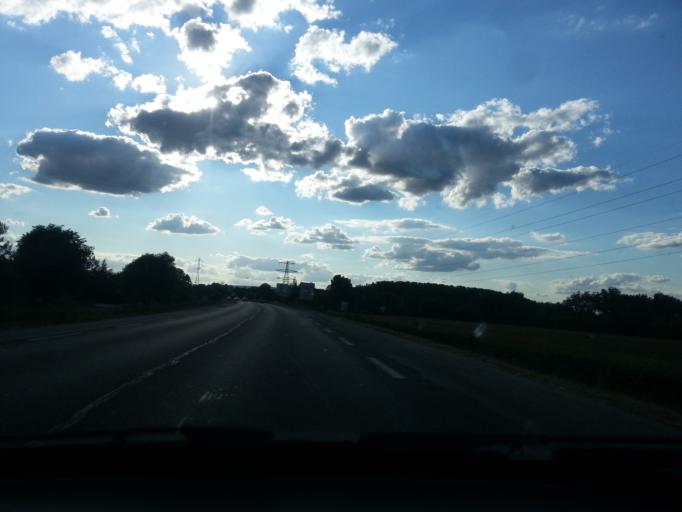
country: FR
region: Bourgogne
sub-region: Departement de Saone-et-Loire
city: Saint-Remy
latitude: 46.7584
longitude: 4.8501
